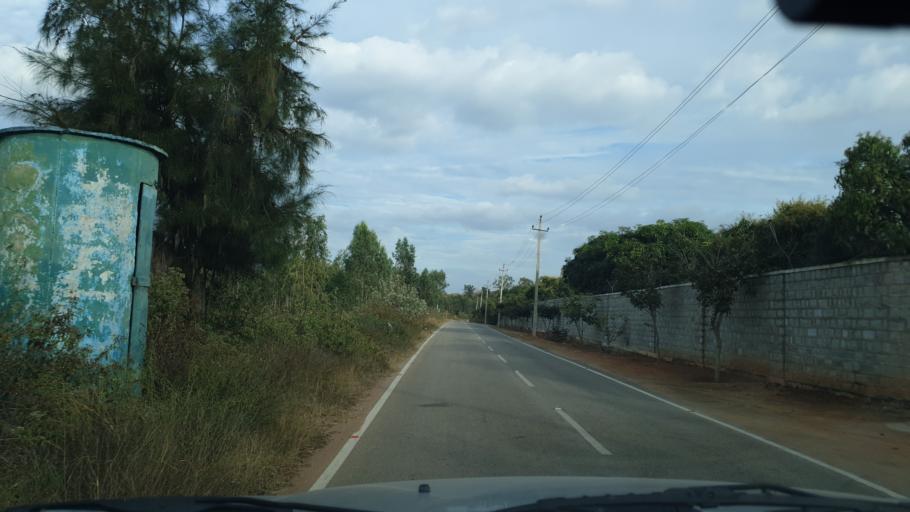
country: IN
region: Karnataka
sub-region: Bangalore Urban
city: Yelahanka
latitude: 13.2020
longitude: 77.6068
